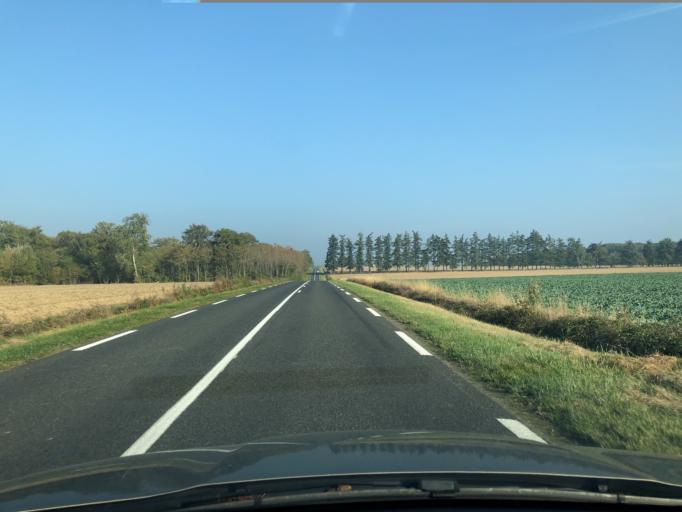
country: FR
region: Centre
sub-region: Departement d'Indre-et-Loire
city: Cerelles
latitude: 47.5229
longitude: 0.6940
